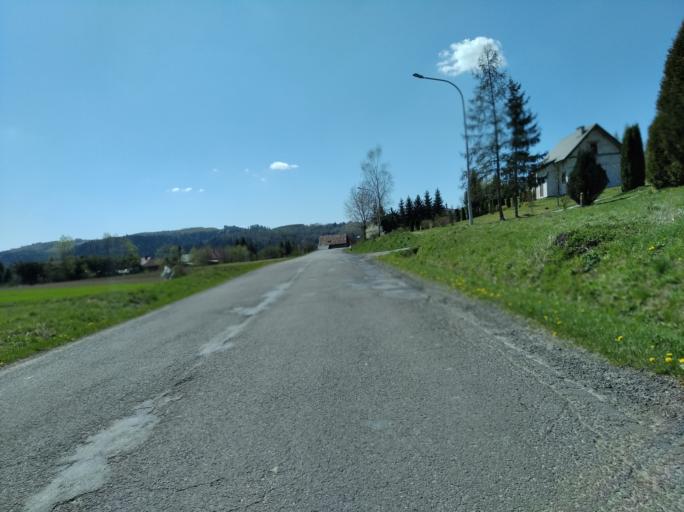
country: PL
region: Subcarpathian Voivodeship
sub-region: Powiat brzozowski
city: Dydnia
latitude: 49.7072
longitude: 22.1975
